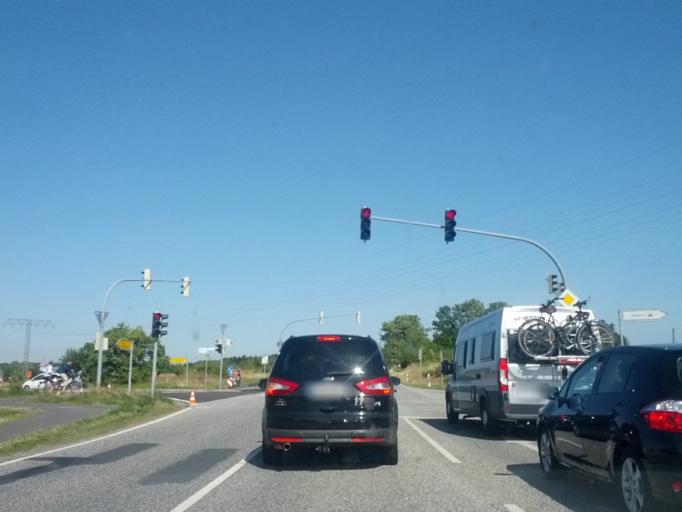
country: DE
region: Mecklenburg-Vorpommern
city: Sagard
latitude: 54.4922
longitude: 13.5790
